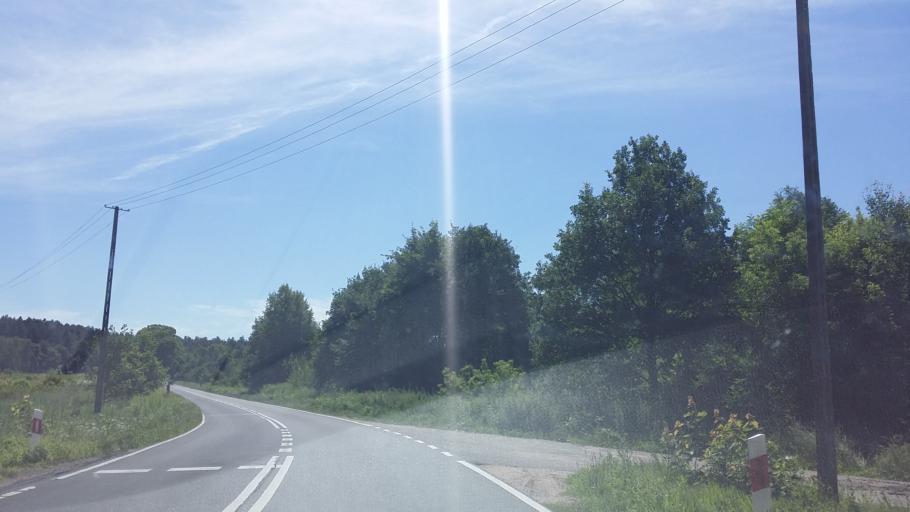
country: PL
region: West Pomeranian Voivodeship
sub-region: Powiat lobeski
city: Lobez
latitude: 53.6743
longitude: 15.6582
